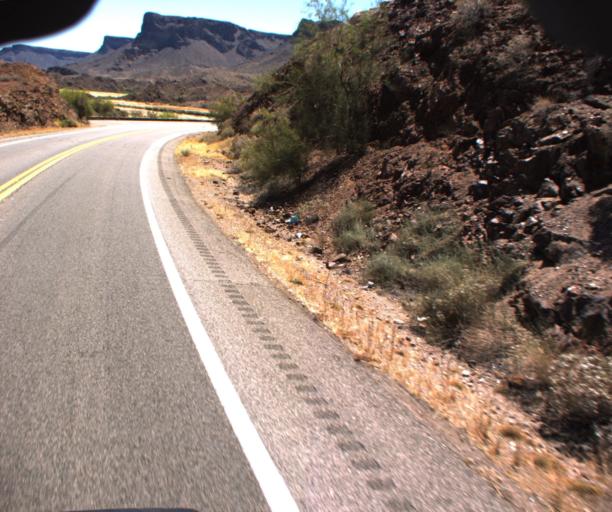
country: US
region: Arizona
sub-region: La Paz County
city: Cienega Springs
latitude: 34.3035
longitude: -114.0942
